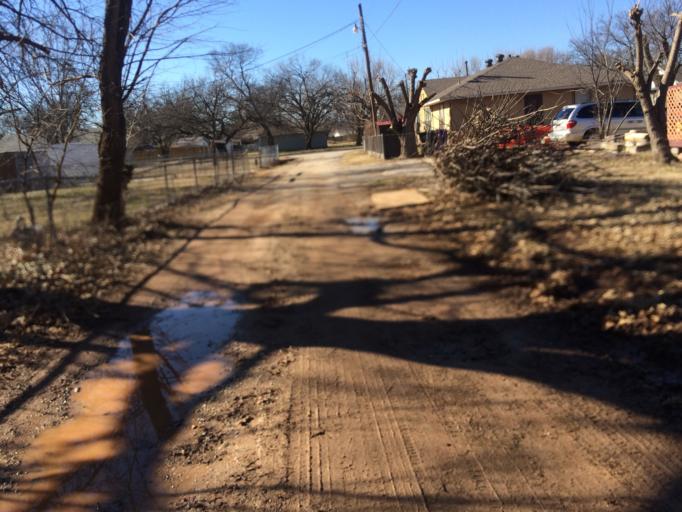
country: US
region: Oklahoma
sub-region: Cleveland County
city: Norman
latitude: 35.2237
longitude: -97.4300
